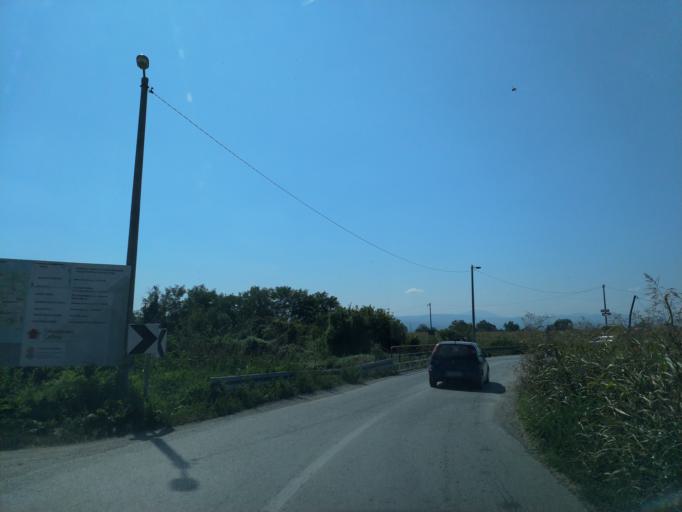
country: RS
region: Central Serbia
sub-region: Rasinski Okrug
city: Trstenik
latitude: 43.6263
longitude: 21.1481
